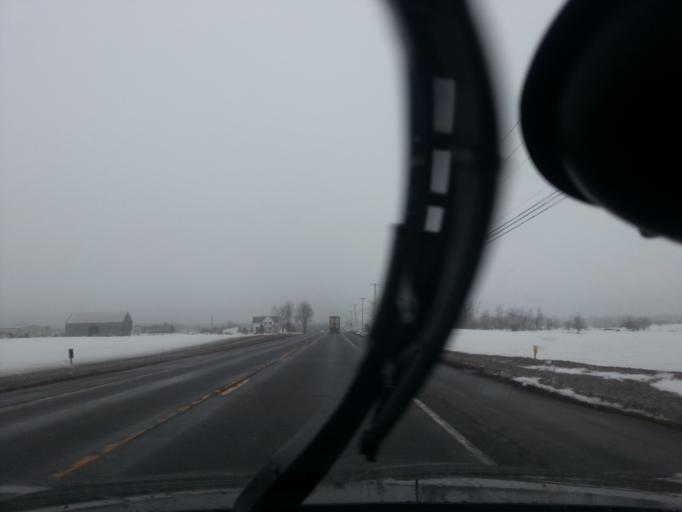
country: US
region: New York
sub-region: Jefferson County
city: Philadelphia
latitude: 44.1247
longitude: -75.7418
